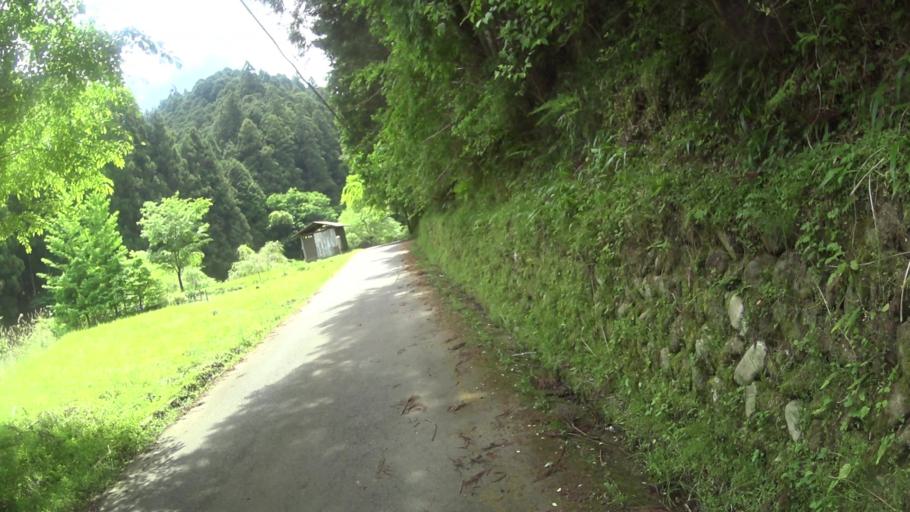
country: JP
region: Nara
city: Yoshino-cho
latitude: 34.3662
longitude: 135.8644
